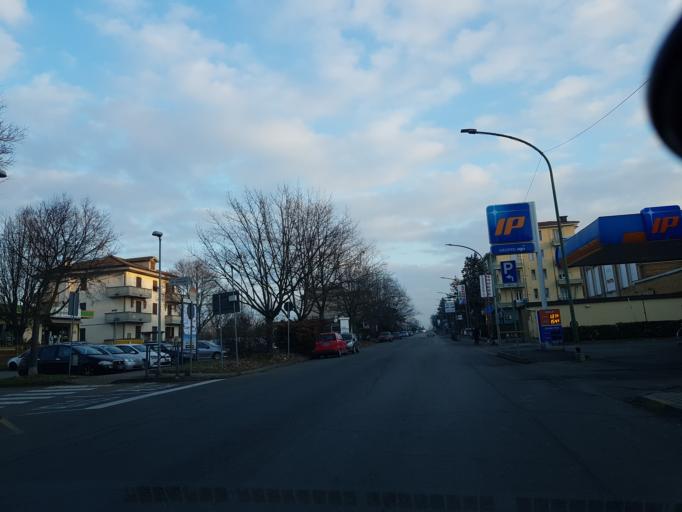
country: IT
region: Piedmont
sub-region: Provincia di Alessandria
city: Novi Ligure
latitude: 44.7584
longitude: 8.7940
